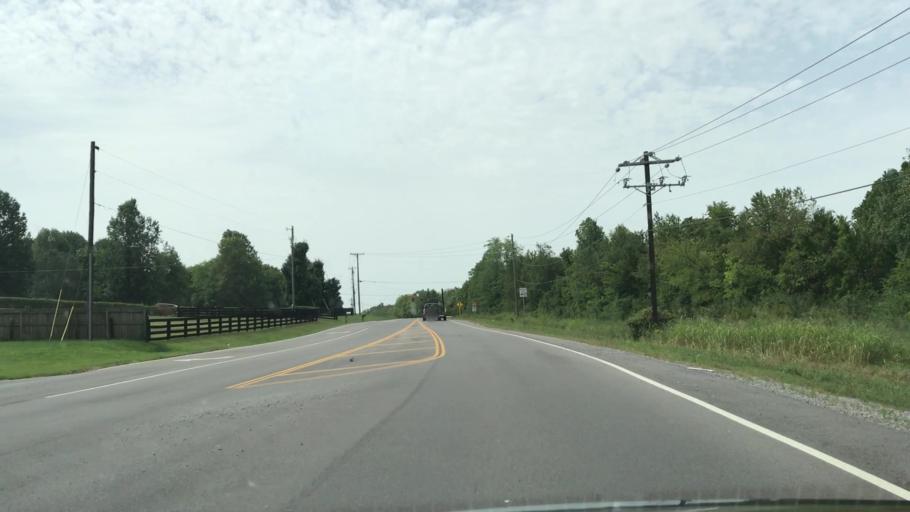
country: US
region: Tennessee
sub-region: Williamson County
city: Brentwood Estates
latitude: 35.9401
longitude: -86.7679
